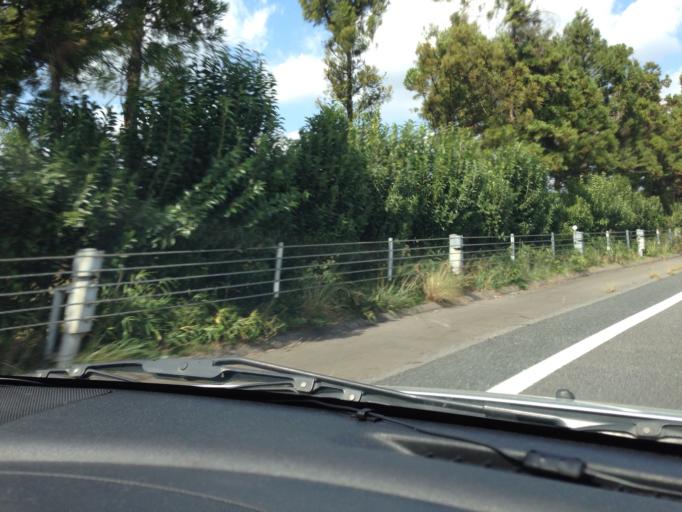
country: JP
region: Ibaraki
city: Mito-shi
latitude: 36.3945
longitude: 140.3882
